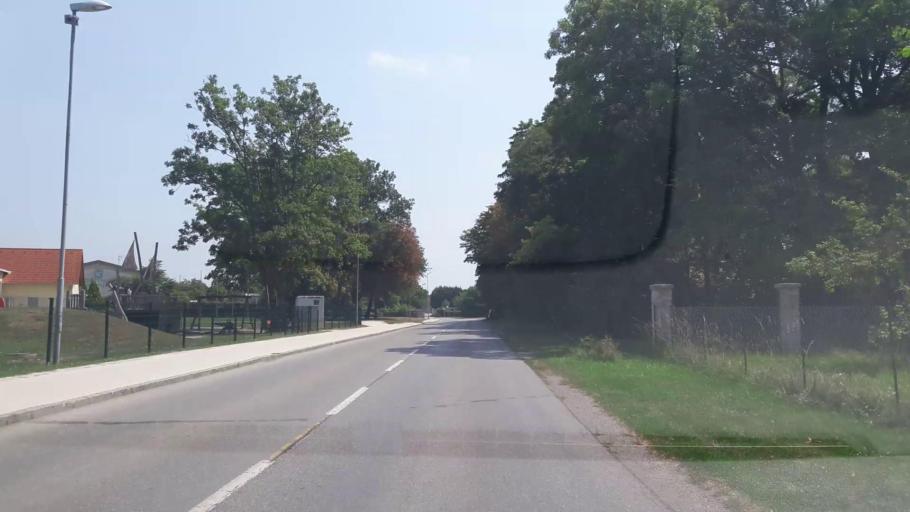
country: AT
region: Lower Austria
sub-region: Politischer Bezirk Bruck an der Leitha
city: Trautmannsdorf an der Leitha
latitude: 48.0235
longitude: 16.6427
